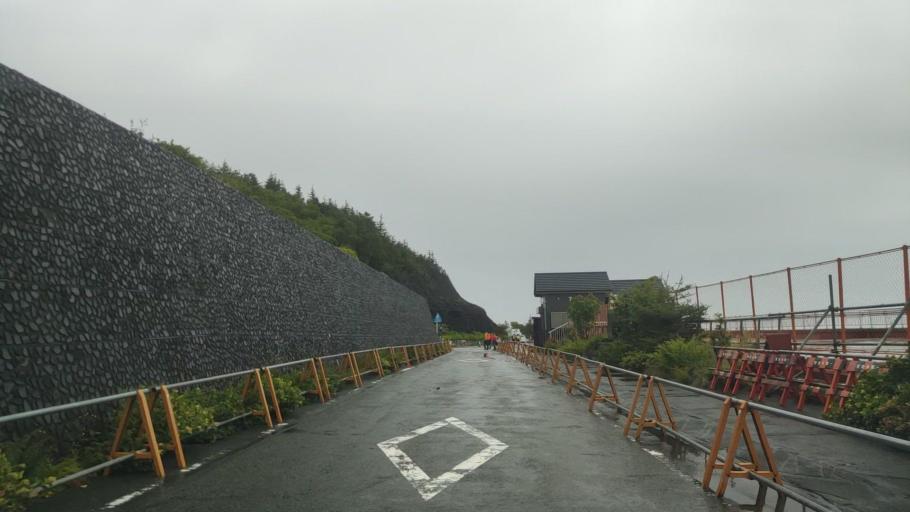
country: JP
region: Yamanashi
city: Fujikawaguchiko
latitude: 35.3368
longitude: 138.7334
